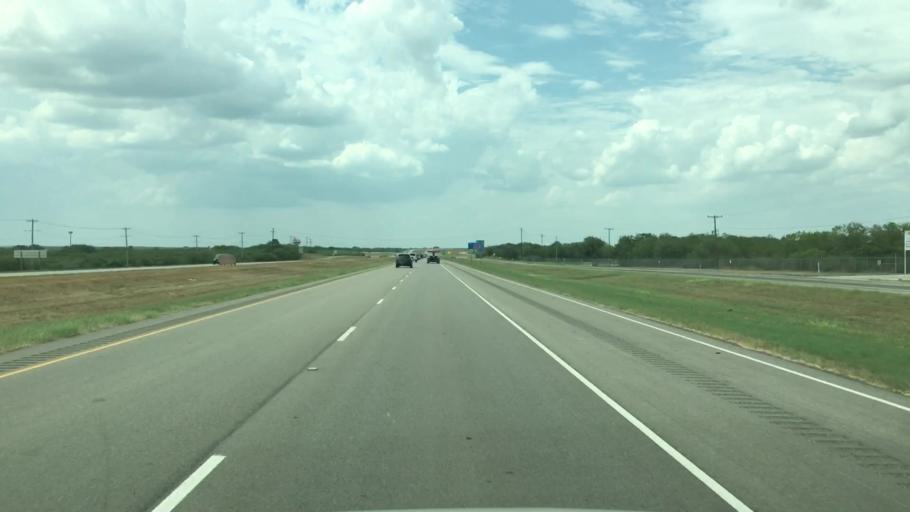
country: US
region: Texas
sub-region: Live Oak County
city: Three Rivers
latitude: 28.5139
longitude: -98.1724
